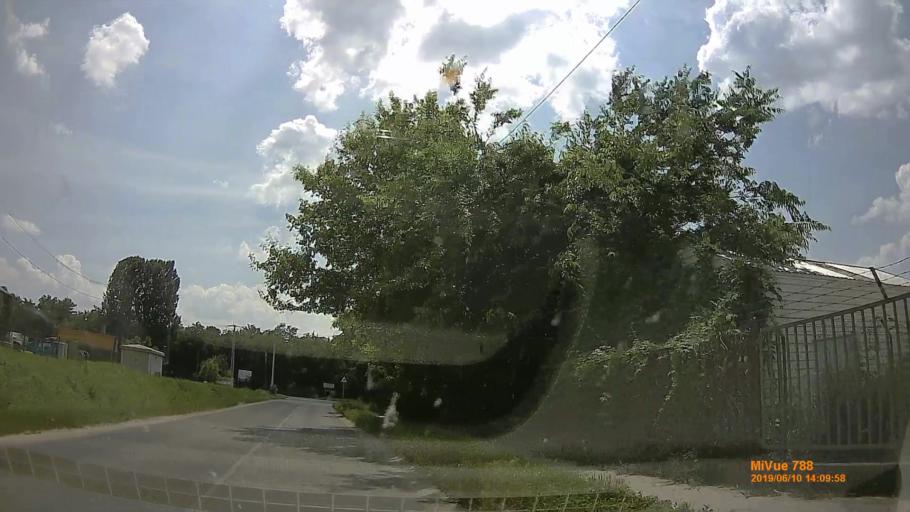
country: HU
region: Pest
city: God
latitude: 47.6785
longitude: 19.1483
